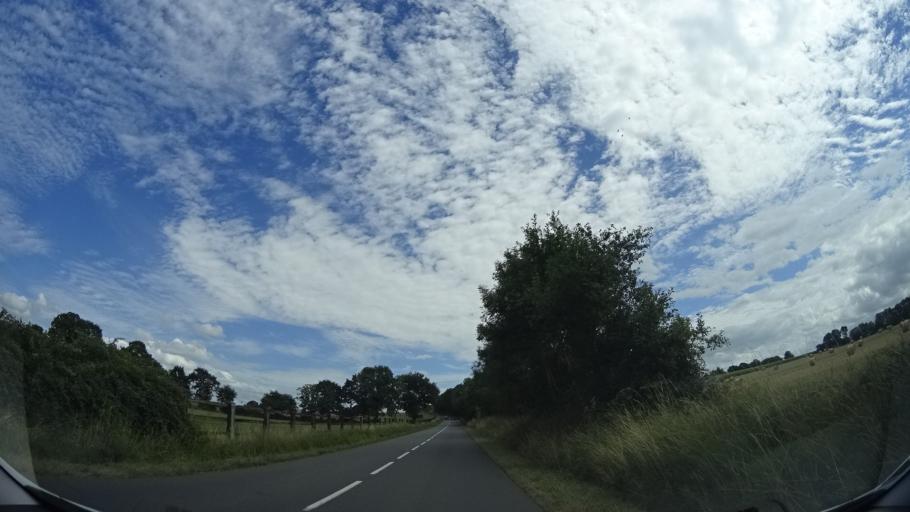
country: FR
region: Lower Normandy
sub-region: Departement de la Manche
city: Marcey-les-Greves
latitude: 48.6841
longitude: -1.4200
